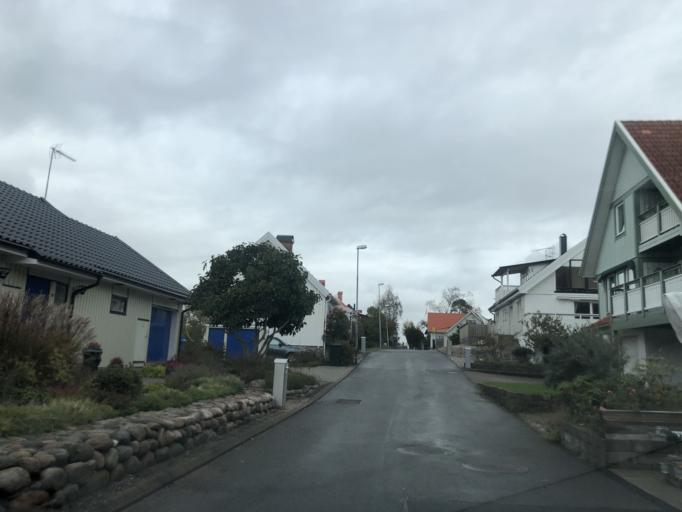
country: SE
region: Vaestra Goetaland
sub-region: Goteborg
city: Majorna
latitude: 57.6732
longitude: 11.8913
